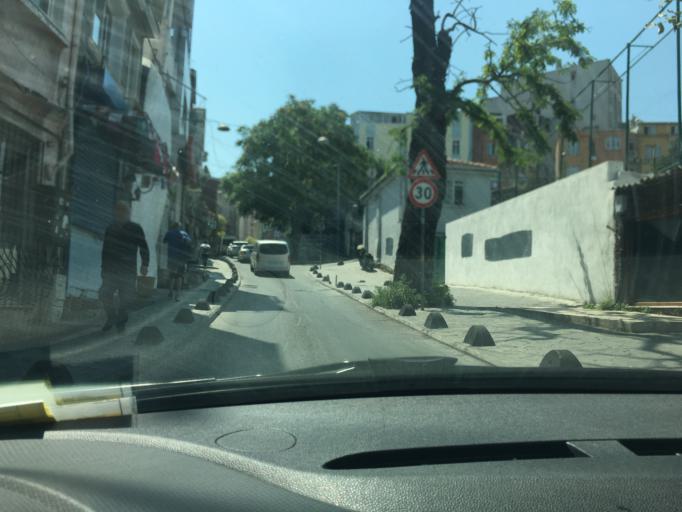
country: TR
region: Istanbul
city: Eminoenue
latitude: 41.0386
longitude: 28.9743
